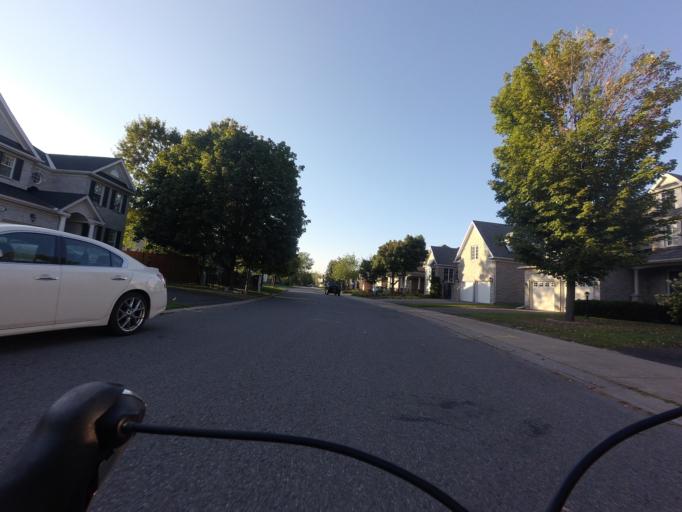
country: CA
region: Ontario
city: Bells Corners
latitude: 45.2589
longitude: -75.7274
